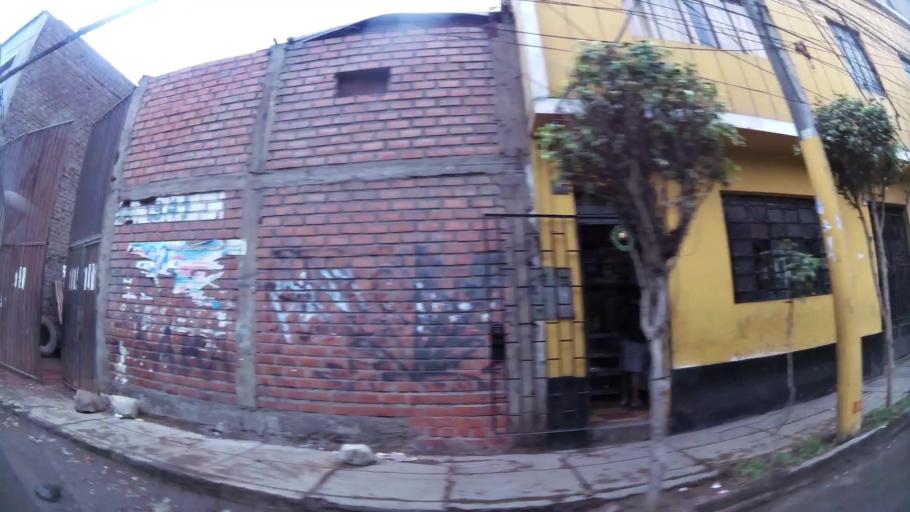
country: PE
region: Lima
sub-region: Lima
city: San Luis
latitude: -12.0687
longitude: -77.0084
